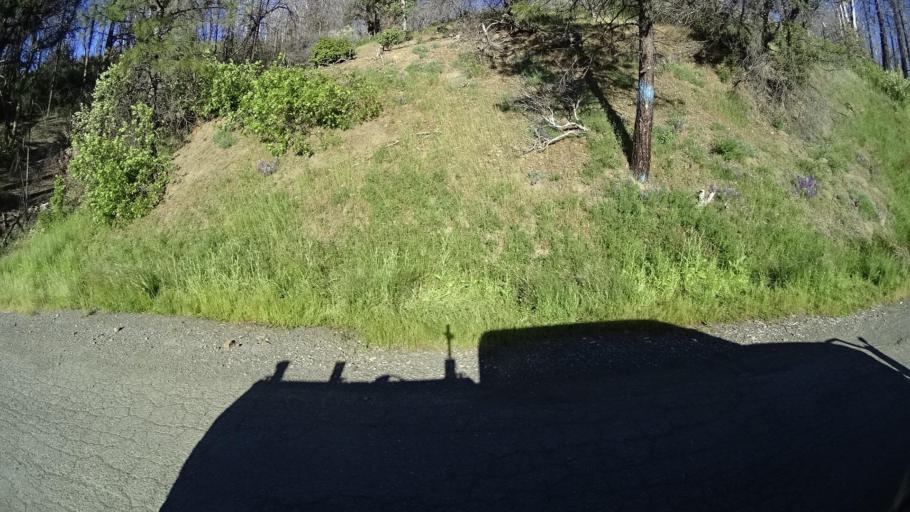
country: US
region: California
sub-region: Lake County
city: Upper Lake
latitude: 39.2819
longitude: -122.9281
